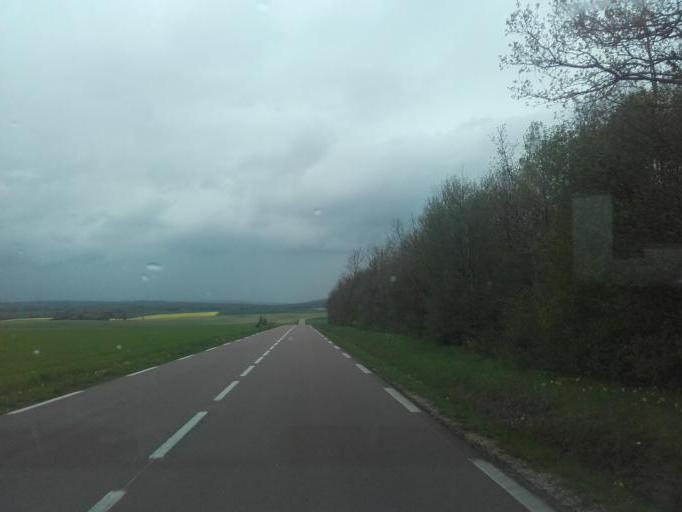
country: FR
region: Bourgogne
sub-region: Departement de l'Yonne
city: Joux-la-Ville
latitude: 47.7054
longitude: 3.8568
